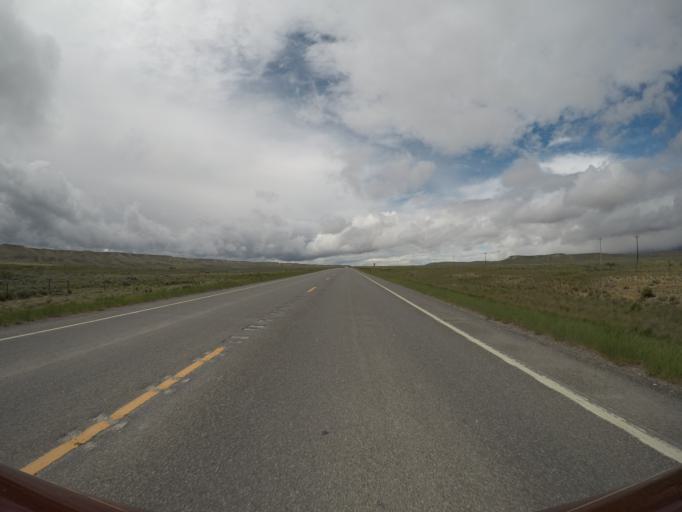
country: US
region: Wyoming
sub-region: Park County
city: Powell
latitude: 45.0270
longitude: -108.6349
